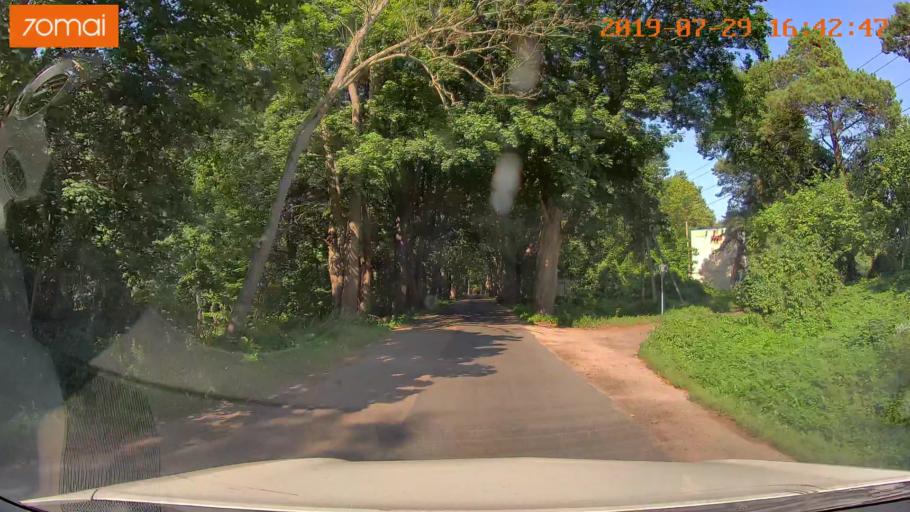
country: RU
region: Kaliningrad
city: Primorsk
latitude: 54.7450
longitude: 20.0772
